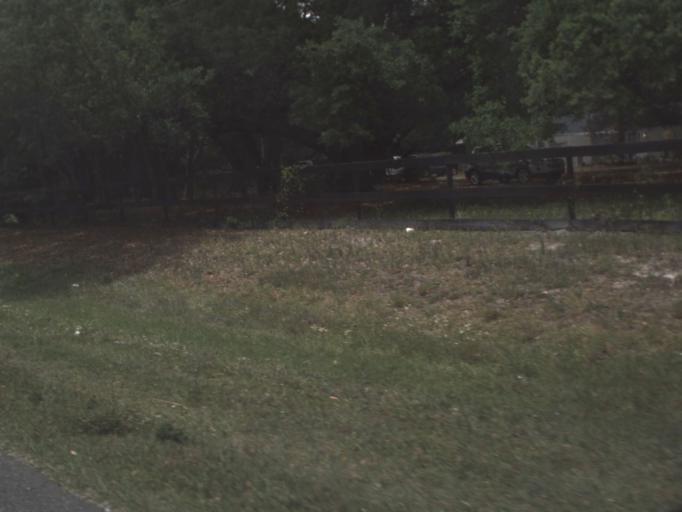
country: US
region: Florida
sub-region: Lake County
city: Mount Dora
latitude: 28.8420
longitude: -81.6338
